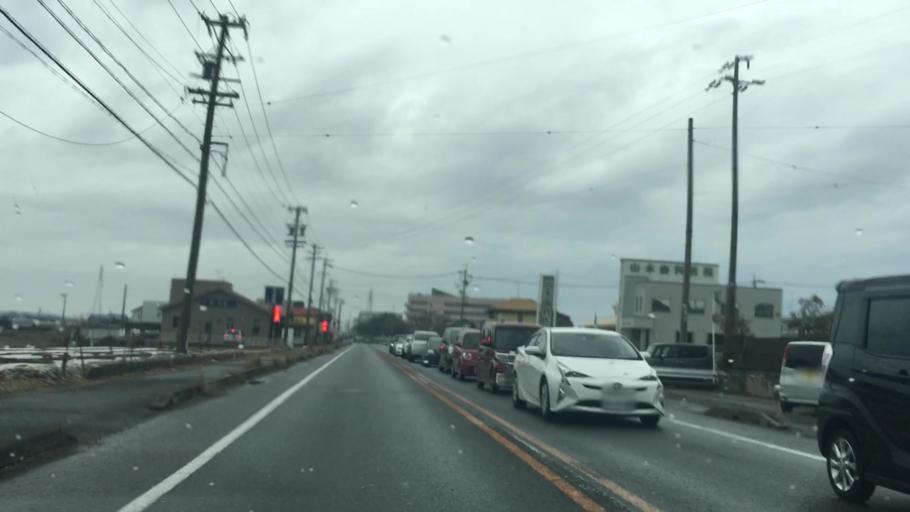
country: JP
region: Aichi
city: Toyohashi
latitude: 34.7230
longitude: 137.4157
